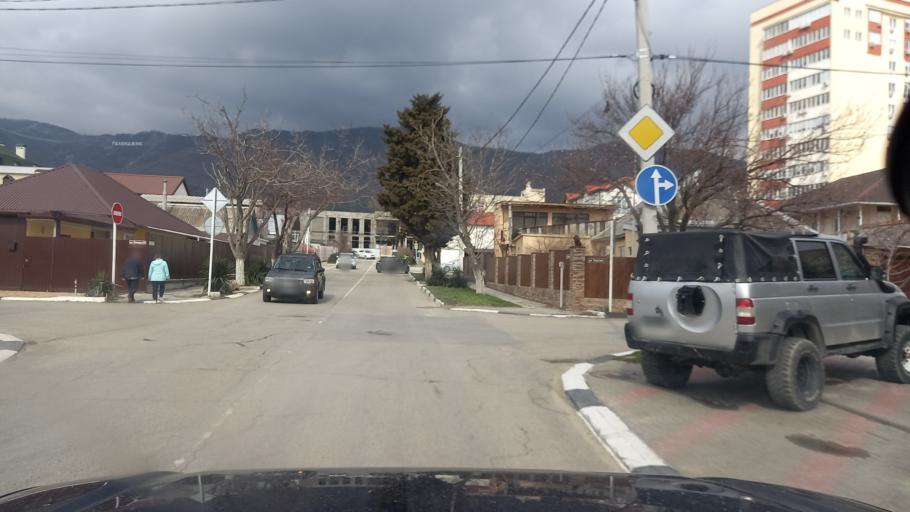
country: RU
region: Krasnodarskiy
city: Gelendzhik
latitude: 44.5600
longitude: 38.0919
